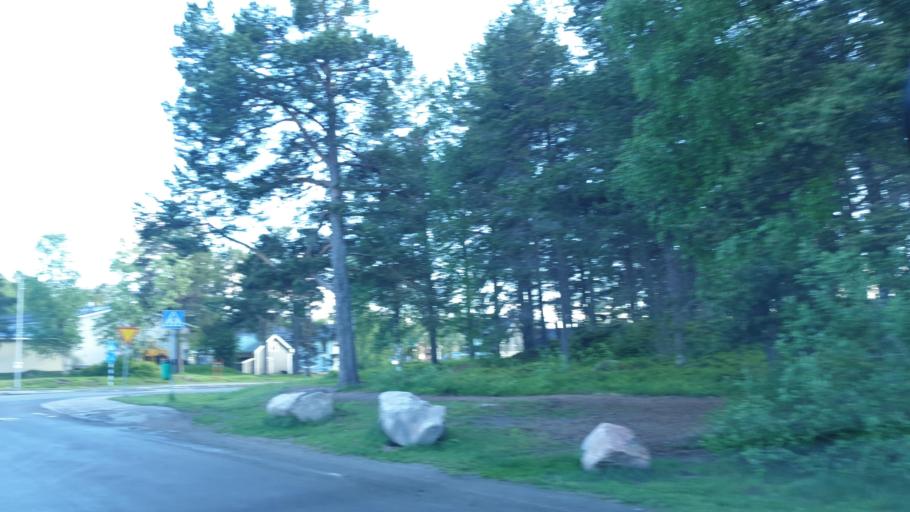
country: SE
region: Norrbotten
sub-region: Arjeplogs Kommun
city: Arjeplog
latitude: 66.0513
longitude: 17.8977
